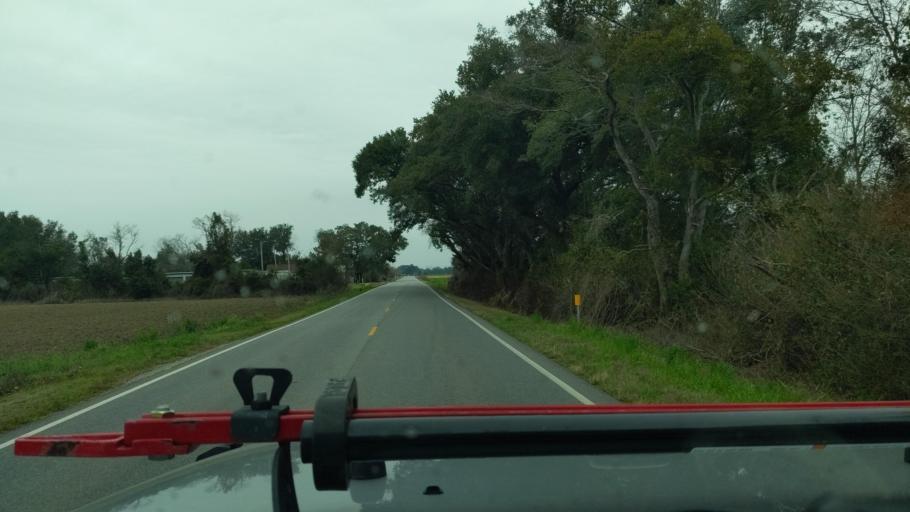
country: US
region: Alabama
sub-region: Baldwin County
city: Foley
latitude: 30.4607
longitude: -87.7424
